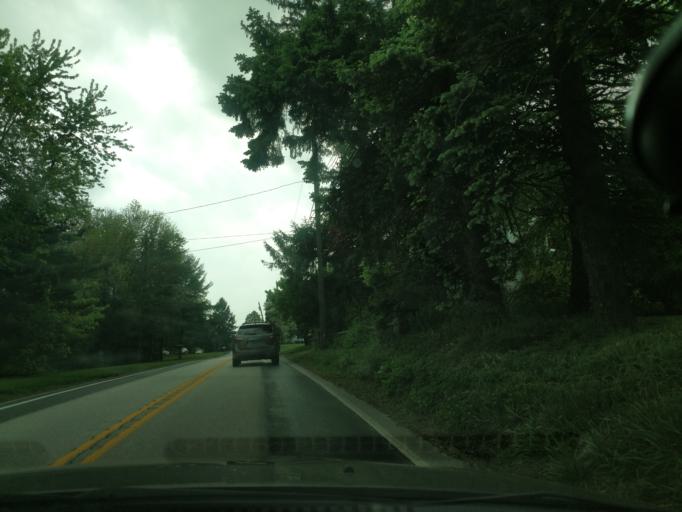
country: US
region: Pennsylvania
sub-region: Chester County
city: Kenilworth
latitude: 40.1776
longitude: -75.6331
